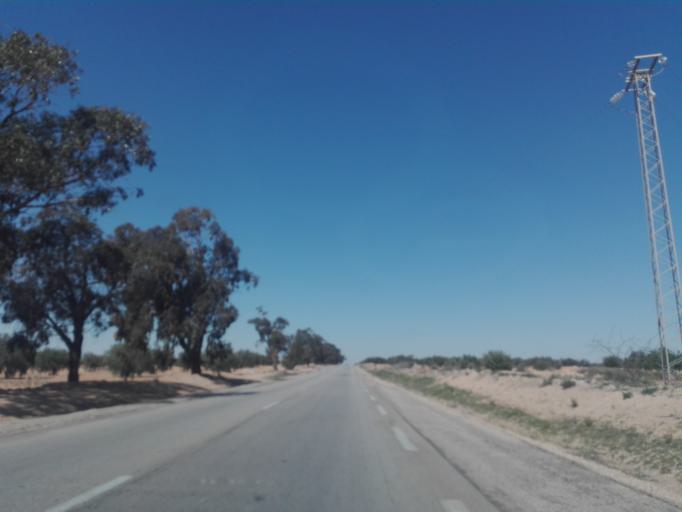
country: TN
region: Safaqis
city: Bi'r `Ali Bin Khalifah
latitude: 34.7580
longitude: 10.3125
